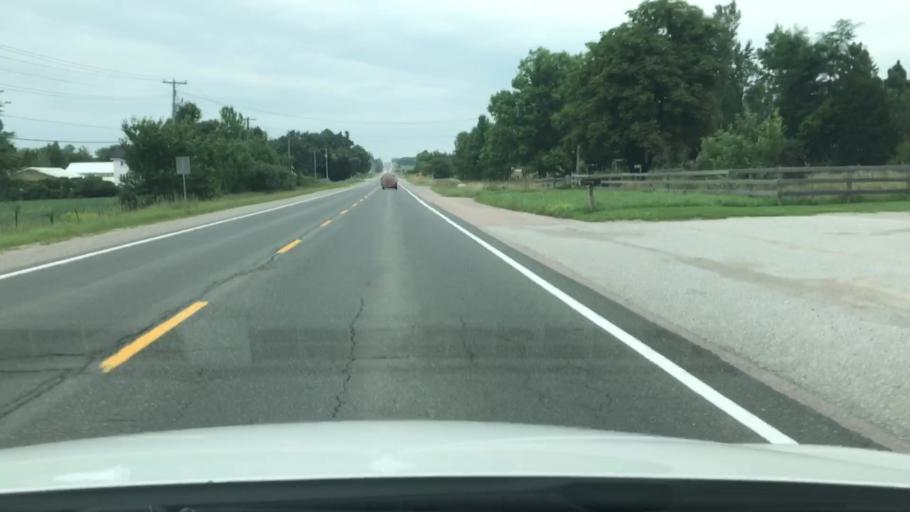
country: CA
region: Ontario
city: Innisfil
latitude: 44.2610
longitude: -79.6033
